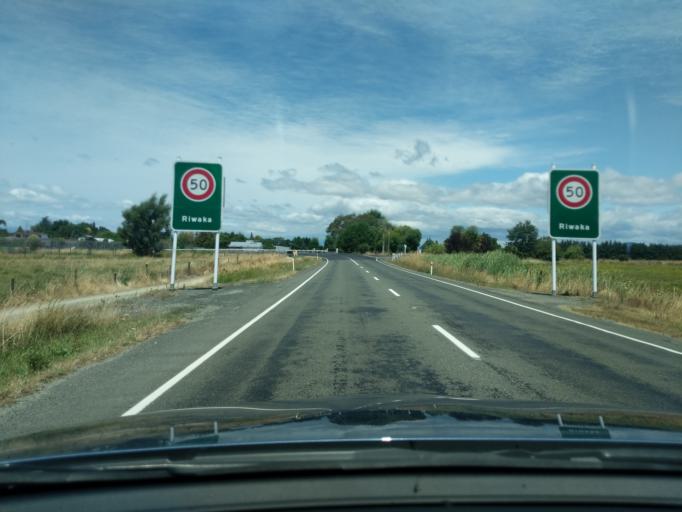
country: NZ
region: Tasman
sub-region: Tasman District
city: Motueka
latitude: -41.0745
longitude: 172.9953
